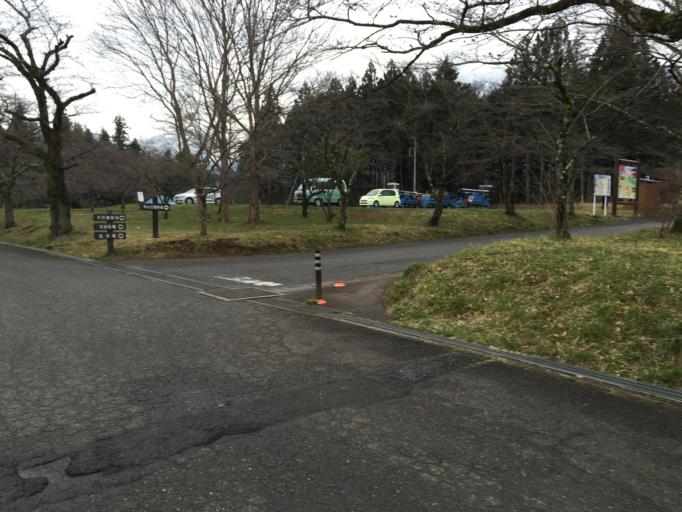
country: JP
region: Saitama
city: Chichibu
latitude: 35.9832
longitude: 139.0875
